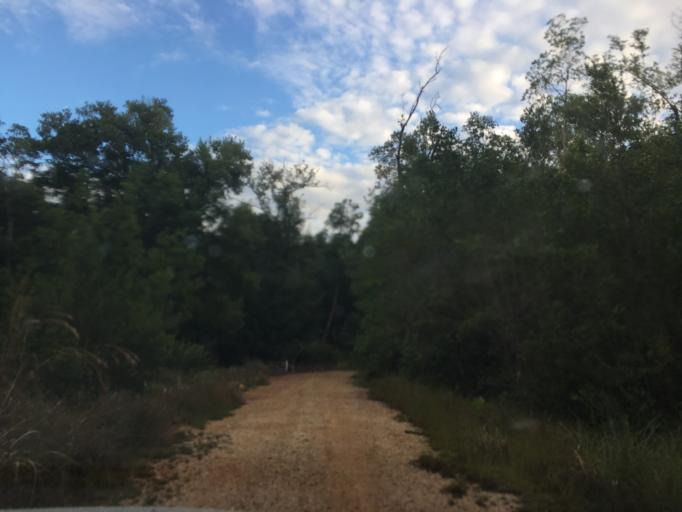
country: BZ
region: Stann Creek
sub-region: Dangriga
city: Dangriga
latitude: 16.8100
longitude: -88.2552
